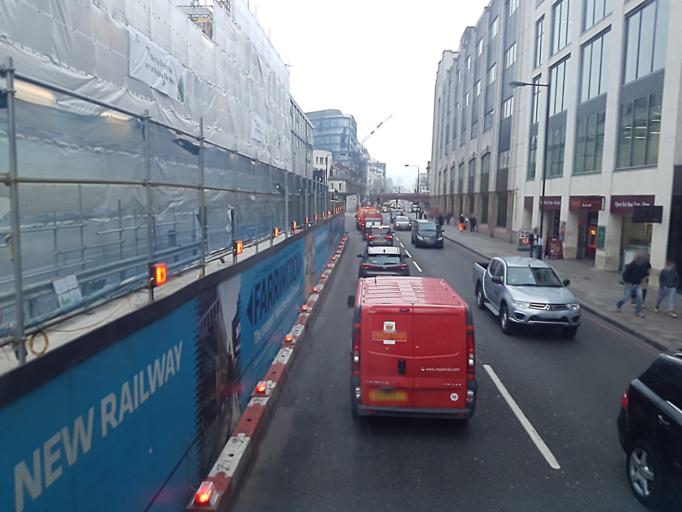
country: GB
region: England
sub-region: Greater London
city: Clerkenwell
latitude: 51.5197
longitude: -0.1056
